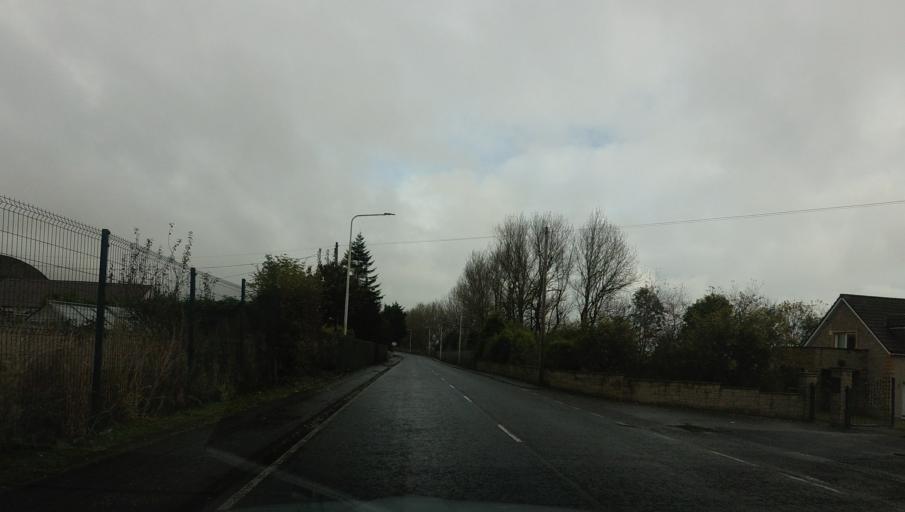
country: GB
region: Scotland
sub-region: Fife
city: Kirkcaldy
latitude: 56.1326
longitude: -3.1185
